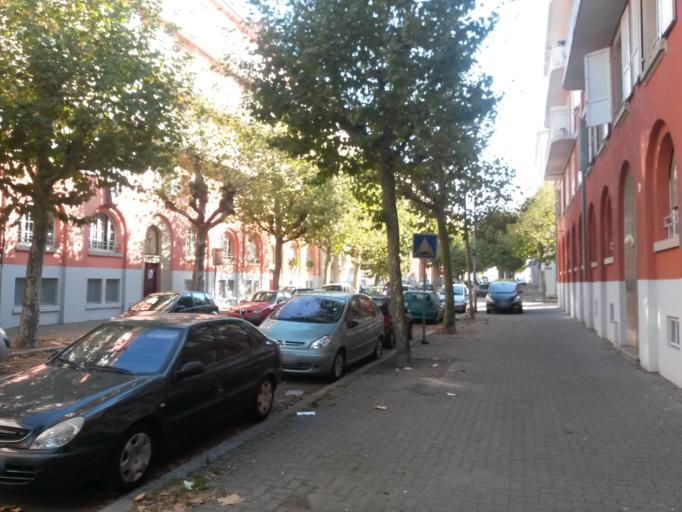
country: DE
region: Baden-Wuerttemberg
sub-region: Freiburg Region
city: Kehl
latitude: 48.5740
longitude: 7.7953
